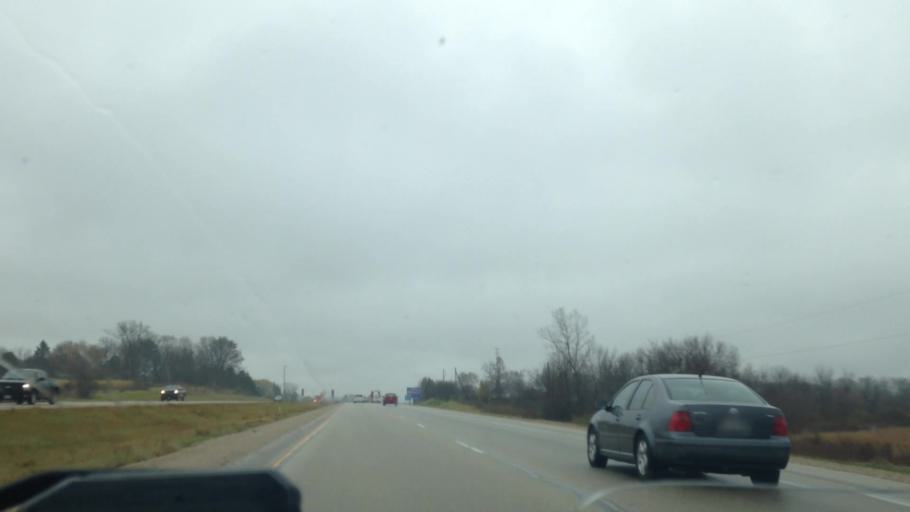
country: US
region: Wisconsin
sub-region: Washington County
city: Richfield
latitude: 43.2918
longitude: -88.2057
